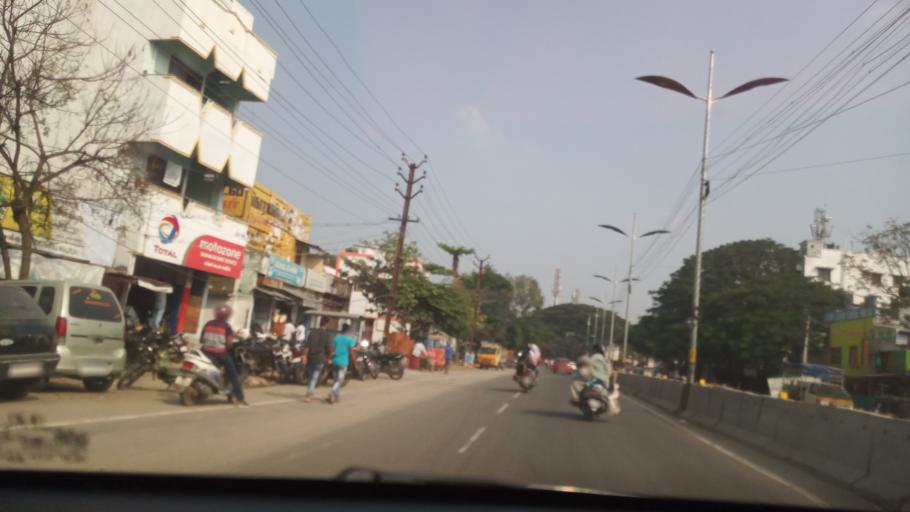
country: IN
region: Tamil Nadu
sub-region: Coimbatore
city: Coimbatore
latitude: 11.0015
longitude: 76.9483
